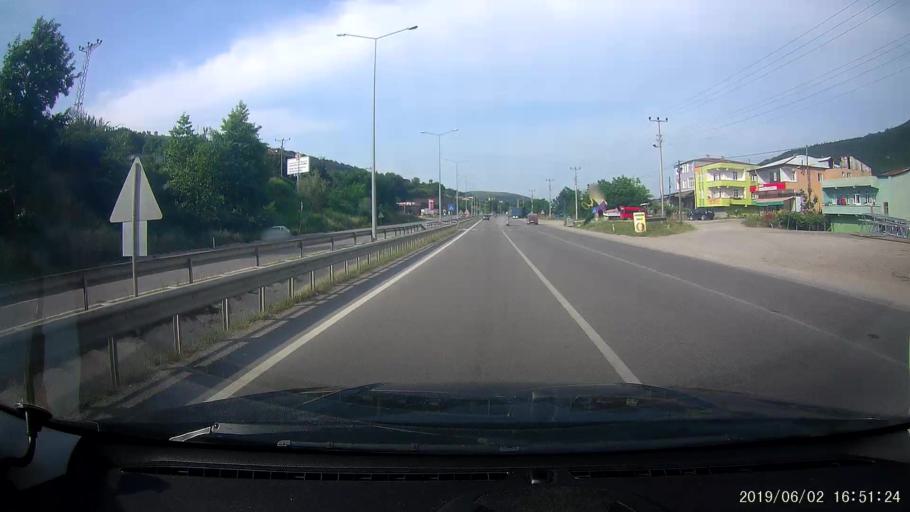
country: TR
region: Samsun
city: Taflan
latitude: 41.2733
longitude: 36.1818
